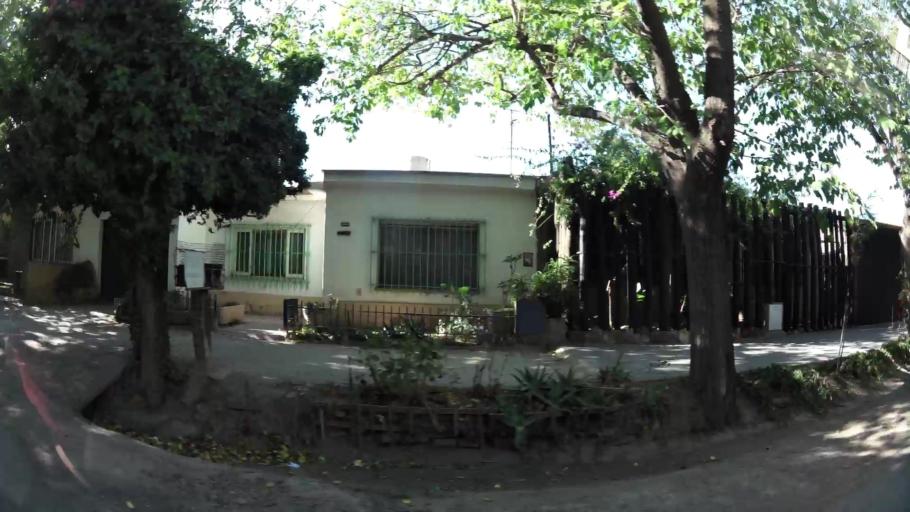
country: AR
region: Mendoza
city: Mendoza
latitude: -32.9039
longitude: -68.8173
